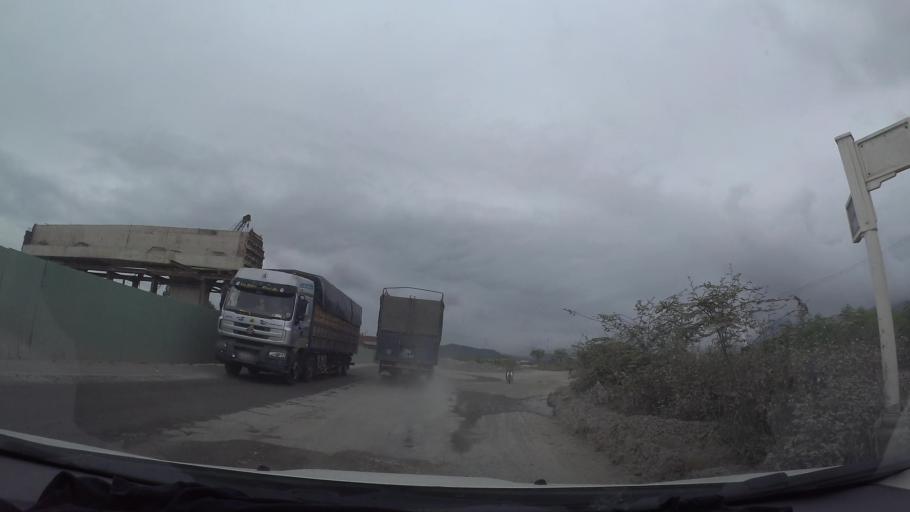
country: VN
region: Da Nang
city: Lien Chieu
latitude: 16.0945
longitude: 108.0878
